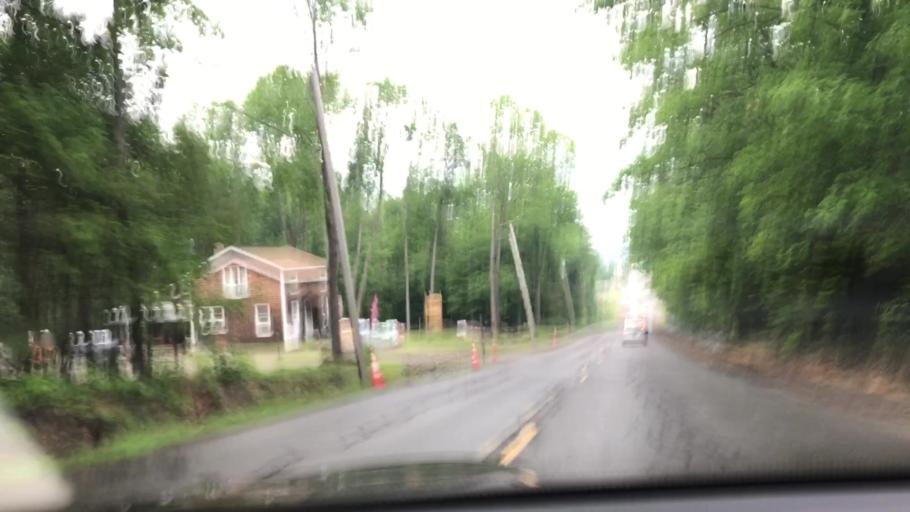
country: US
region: Maine
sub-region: Penobscot County
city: Orono
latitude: 44.8985
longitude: -68.6961
